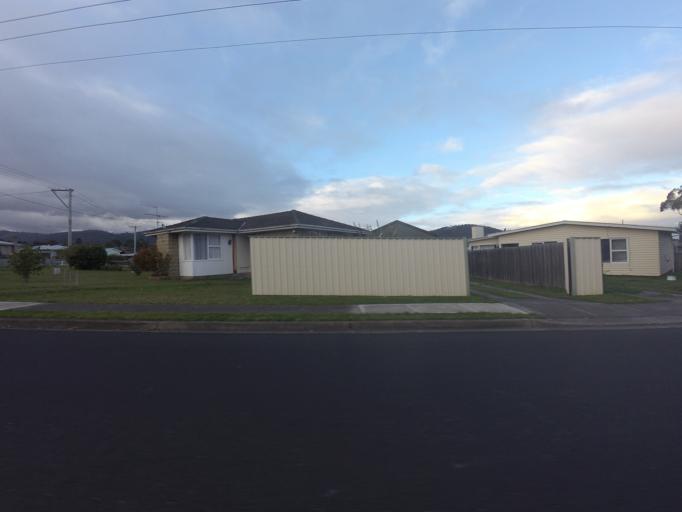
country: AU
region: Tasmania
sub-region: Clarence
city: Rokeby
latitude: -42.8971
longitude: 147.4346
